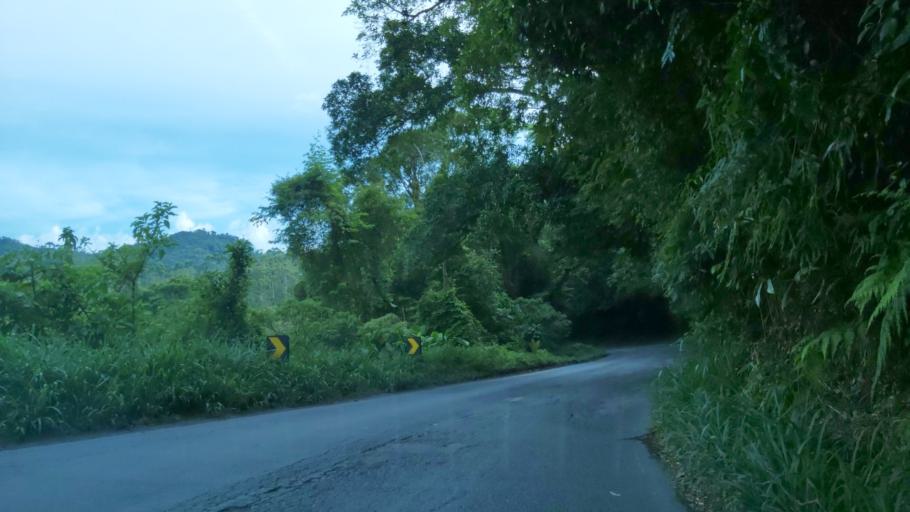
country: BR
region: Sao Paulo
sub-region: Juquia
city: Juquia
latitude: -24.0700
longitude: -47.6034
